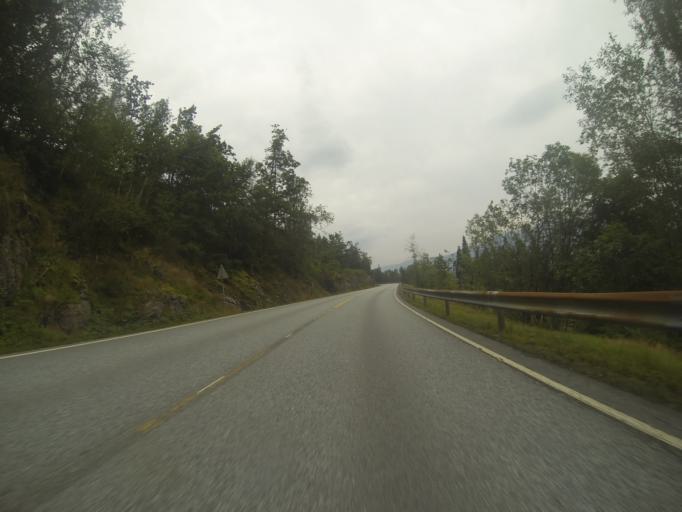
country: NO
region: Rogaland
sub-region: Suldal
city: Sand
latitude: 59.5537
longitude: 6.2612
